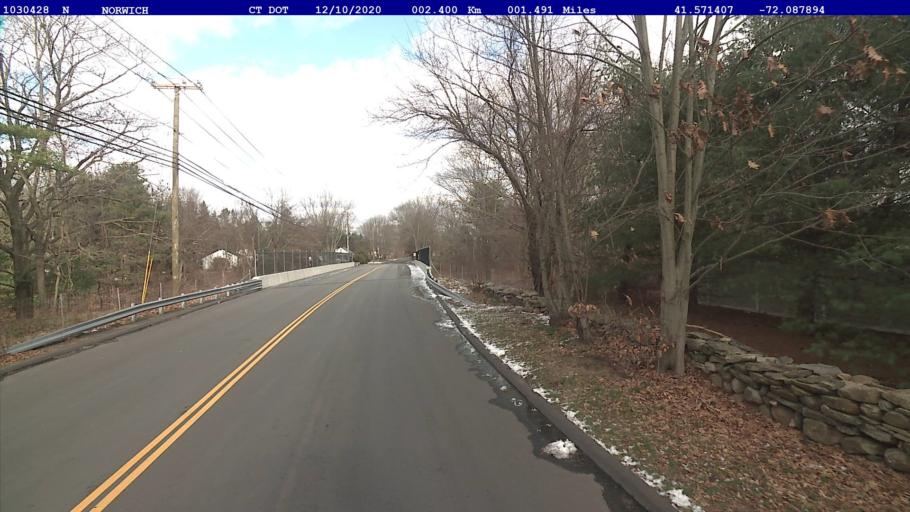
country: US
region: Connecticut
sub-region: New London County
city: Baltic
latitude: 41.5714
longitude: -72.0879
